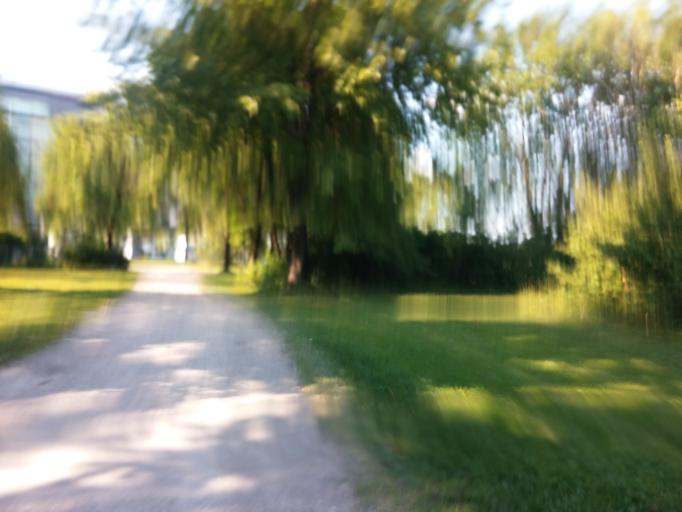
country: DE
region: Bavaria
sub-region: Upper Bavaria
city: Bogenhausen
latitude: 48.1342
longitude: 11.6712
